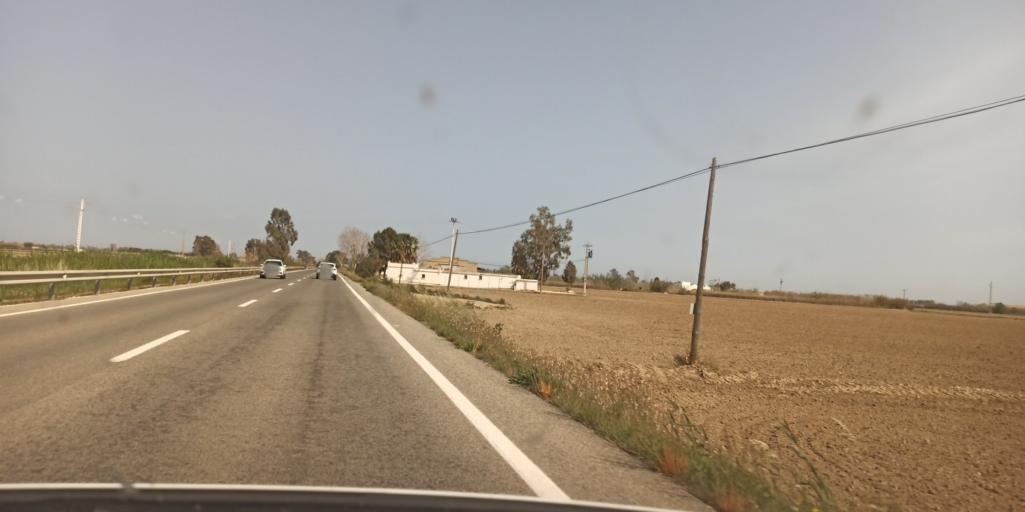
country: ES
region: Catalonia
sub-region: Provincia de Tarragona
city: Deltebre
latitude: 40.7057
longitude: 0.8015
